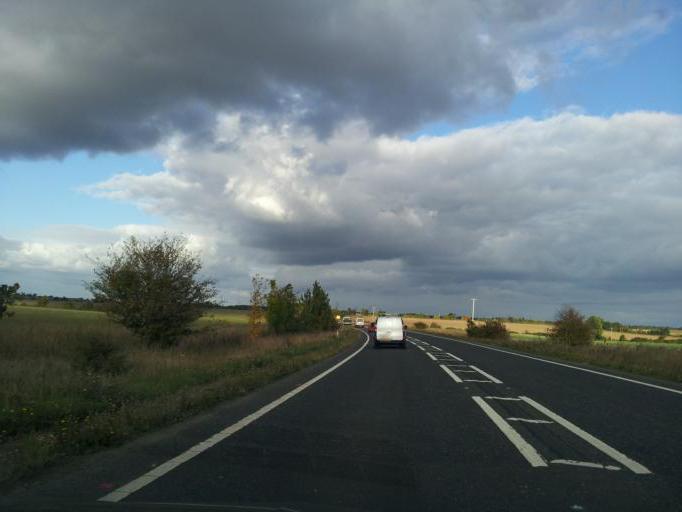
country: GB
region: England
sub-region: Cambridgeshire
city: Saint Neots
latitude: 52.2114
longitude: -0.2519
